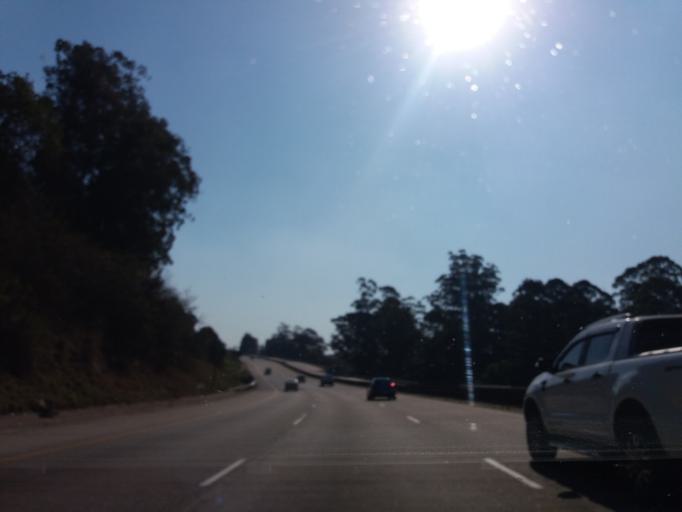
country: ZA
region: KwaZulu-Natal
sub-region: eThekwini Metropolitan Municipality
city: Mpumalanga
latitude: -29.7435
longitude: 30.6624
